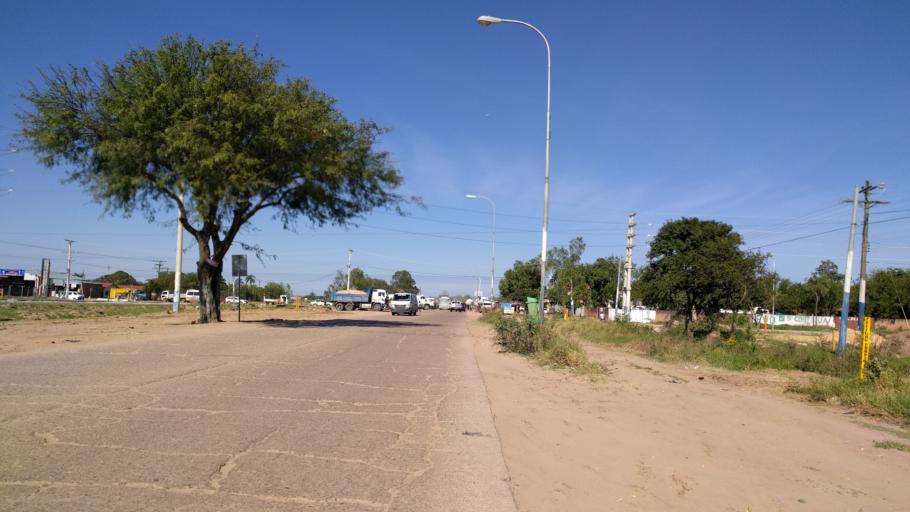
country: BO
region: Santa Cruz
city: Santa Cruz de la Sierra
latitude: -17.8722
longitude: -63.1923
